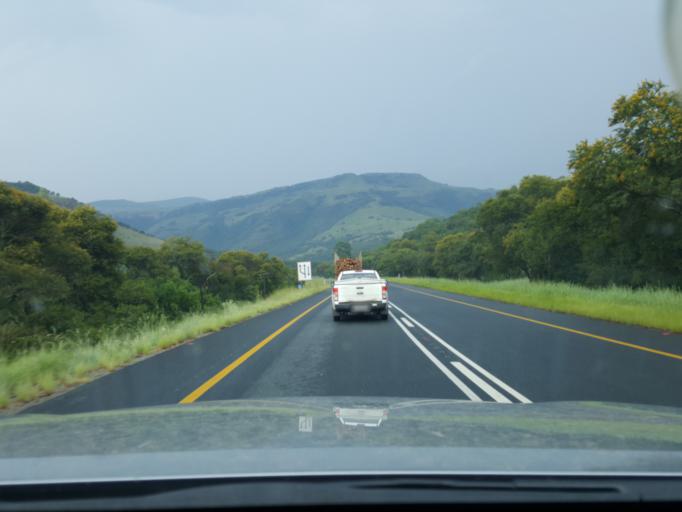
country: ZA
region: Mpumalanga
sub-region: Nkangala District Municipality
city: Belfast
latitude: -25.6286
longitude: 30.3969
